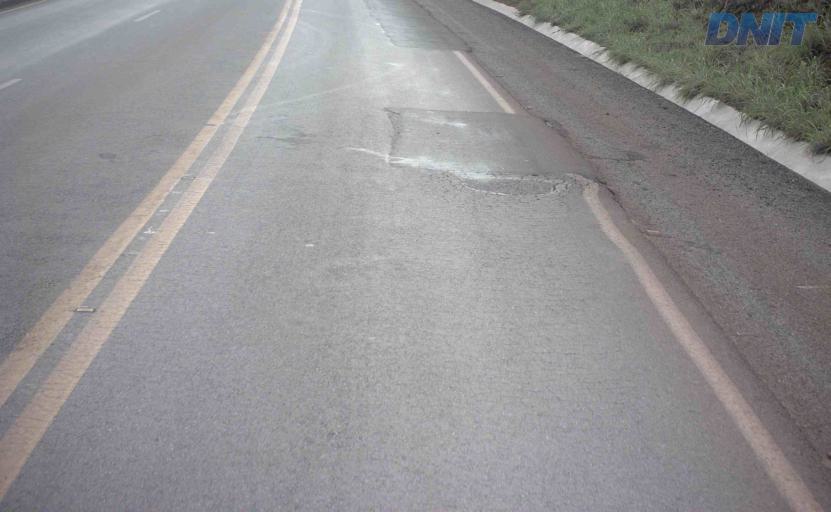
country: BR
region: Goias
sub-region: Barro Alto
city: Barro Alto
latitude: -14.8674
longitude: -49.0137
